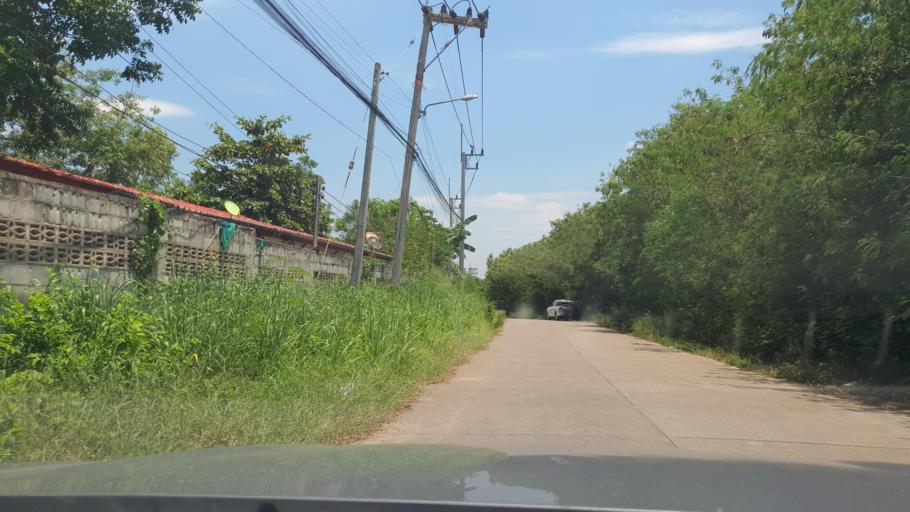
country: TH
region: Chon Buri
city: Phatthaya
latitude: 12.8950
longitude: 100.8801
